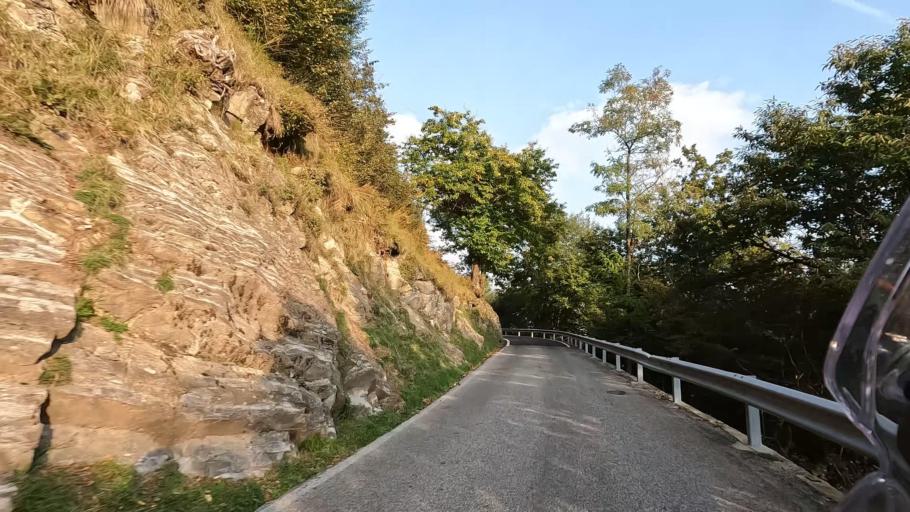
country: IT
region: Lombardy
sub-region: Provincia di Como
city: Dizzasco-Biazzeno
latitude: 45.9509
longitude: 9.1043
